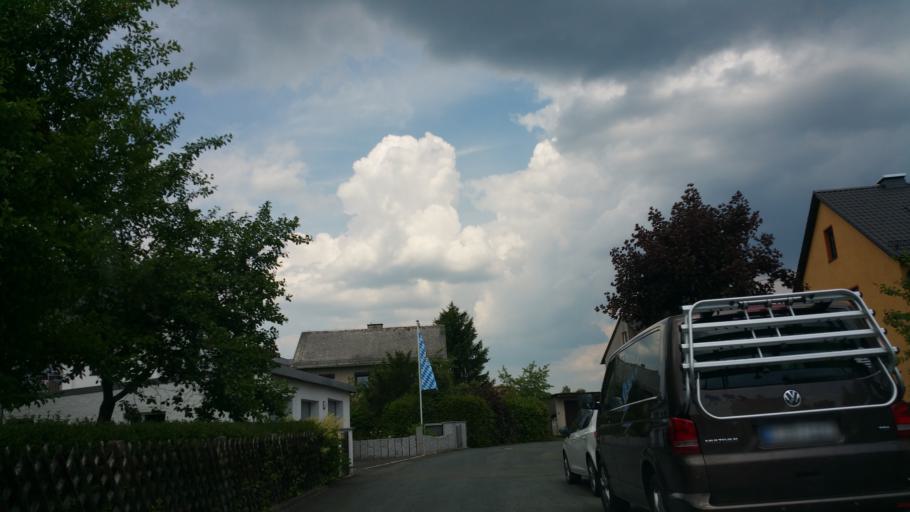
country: DE
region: Bavaria
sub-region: Upper Franconia
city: Schwarzenbach an der Saale
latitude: 50.2193
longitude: 11.9481
